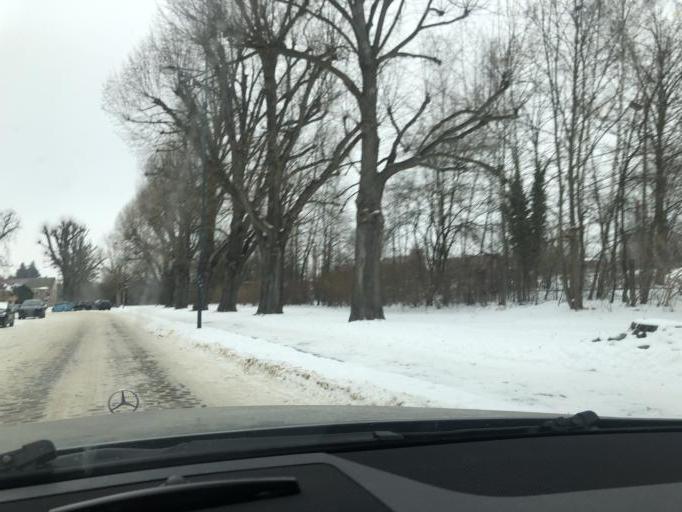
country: DE
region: Brandenburg
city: Guben
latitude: 51.9483
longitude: 14.7093
